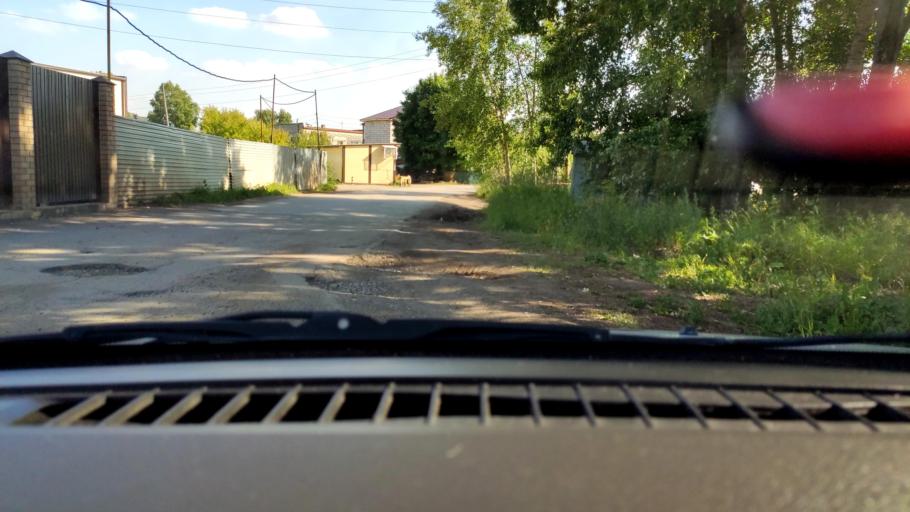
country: RU
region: Perm
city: Kultayevo
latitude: 57.8993
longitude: 55.9429
